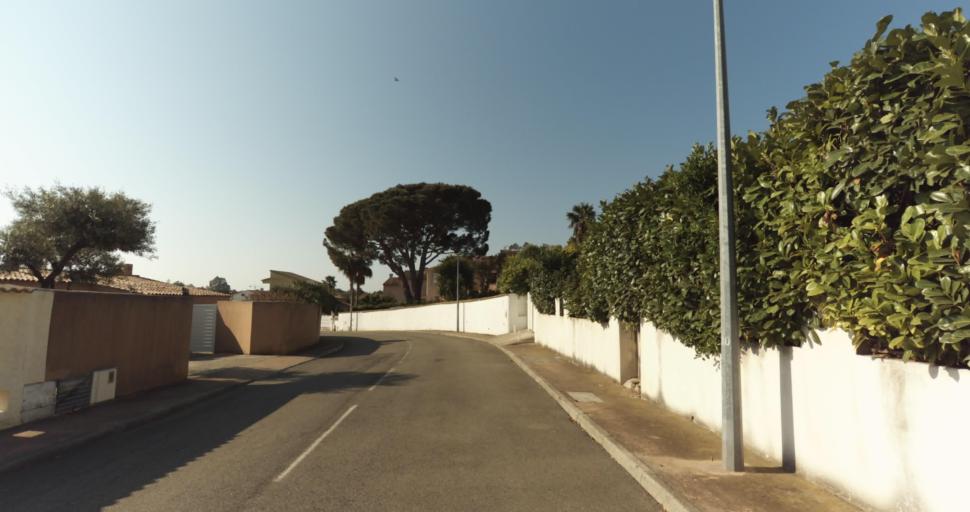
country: FR
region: Corsica
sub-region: Departement de la Haute-Corse
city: Biguglia
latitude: 42.6374
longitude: 9.4303
